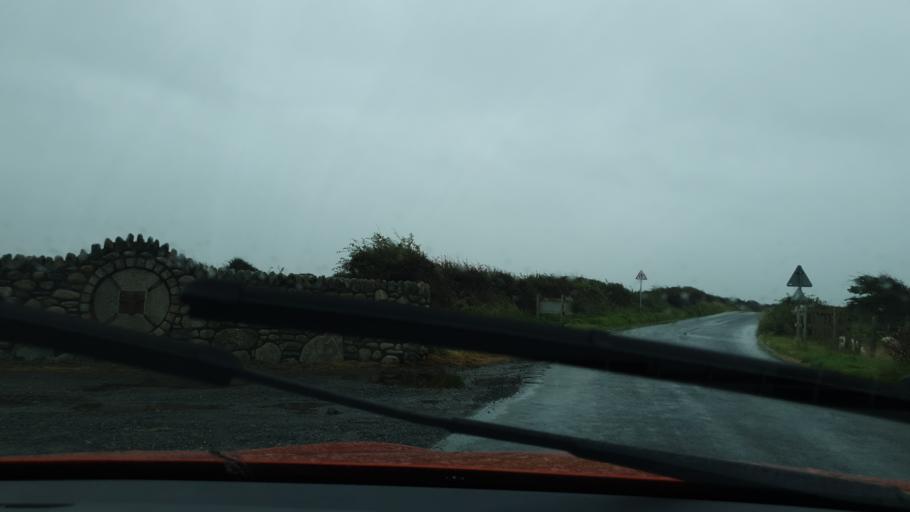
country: GB
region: England
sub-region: Cumbria
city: Barrow in Furness
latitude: 54.0838
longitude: -3.2365
